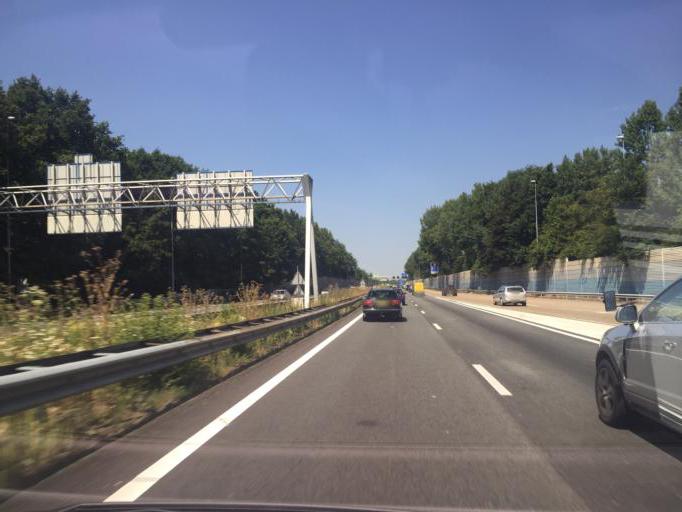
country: NL
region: North Holland
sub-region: Gemeente Aalsmeer
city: Aalsmeer
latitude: 52.3322
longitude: 4.7886
